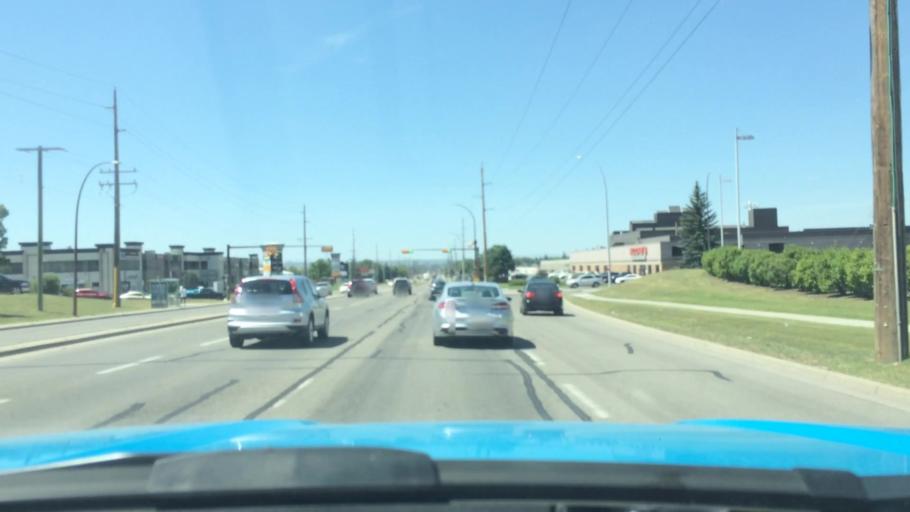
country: CA
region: Alberta
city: Calgary
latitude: 51.0816
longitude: -114.0036
